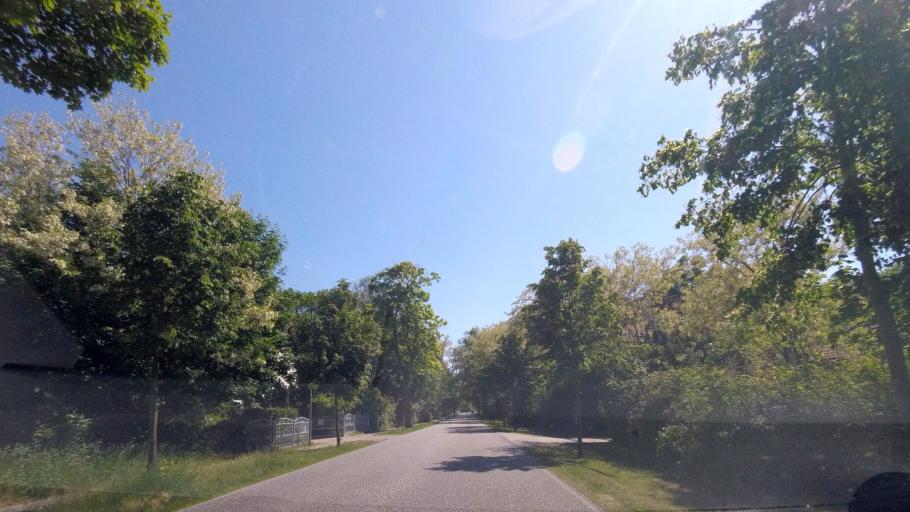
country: DE
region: Brandenburg
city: Gross Kreutz
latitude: 52.3508
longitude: 12.7652
